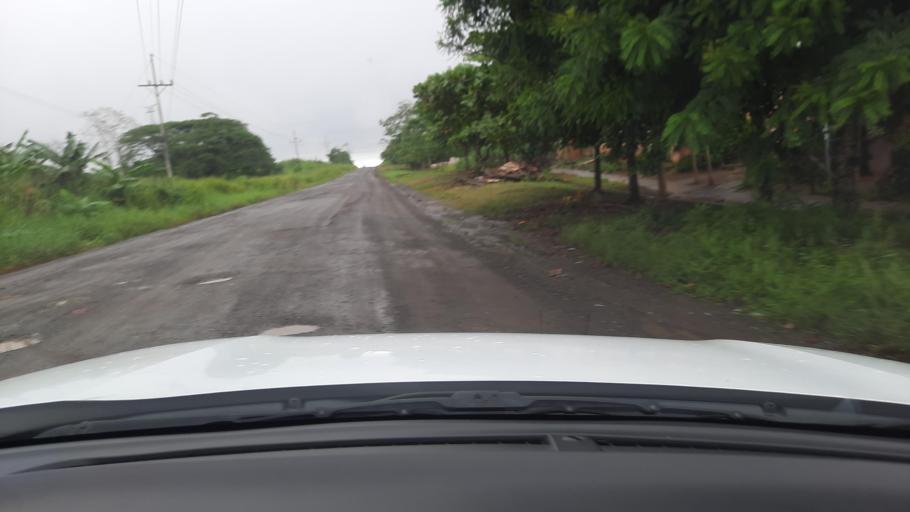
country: CR
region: Alajuela
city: San Jose
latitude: 11.0124
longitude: -85.3412
